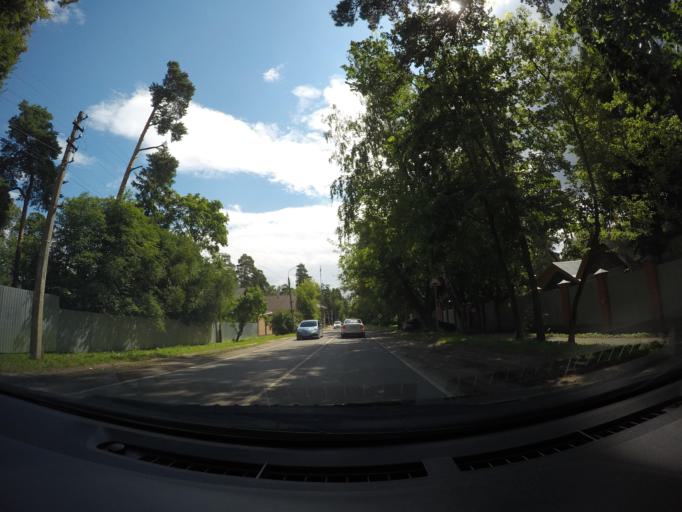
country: RU
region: Moskovskaya
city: Kraskovo
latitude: 55.6552
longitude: 37.9906
